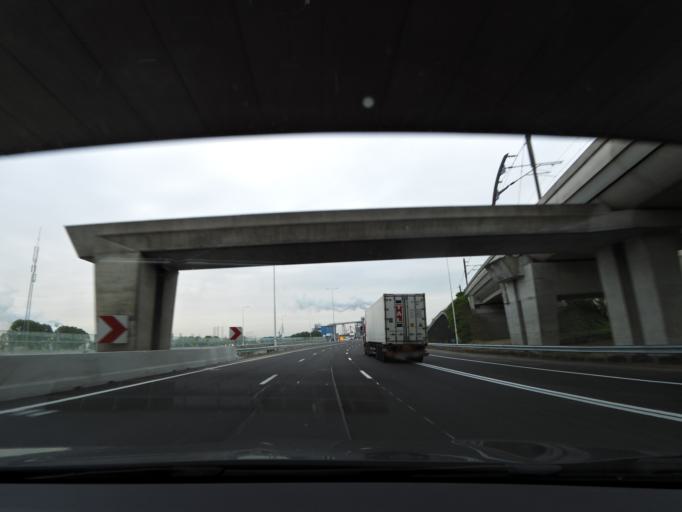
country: NL
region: South Holland
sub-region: Gemeente Maassluis
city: Maassluis
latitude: 51.8958
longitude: 4.2564
